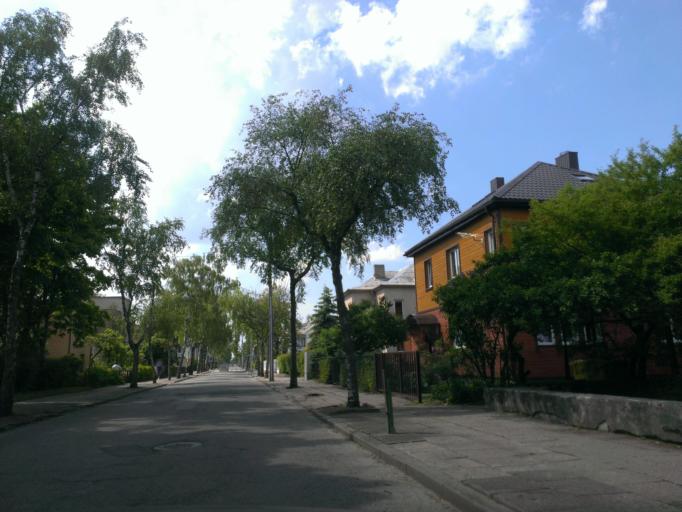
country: LT
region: Klaipedos apskritis
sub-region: Klaipeda
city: Palanga
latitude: 55.9234
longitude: 21.0692
